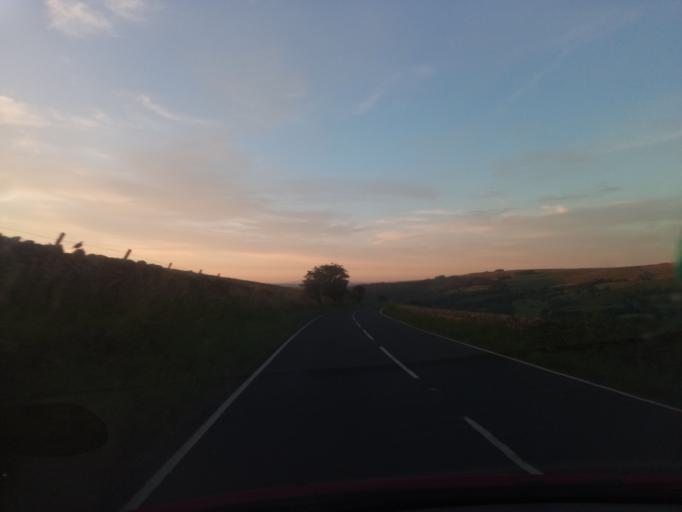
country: GB
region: England
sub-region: Northumberland
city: Bardon Mill
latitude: 54.8679
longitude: -2.3566
